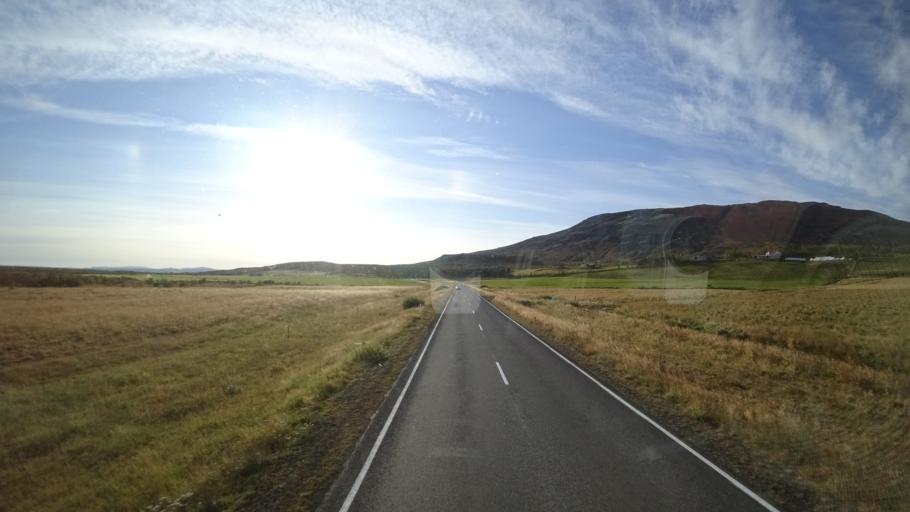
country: IS
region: South
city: Selfoss
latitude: 64.2398
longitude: -20.5400
